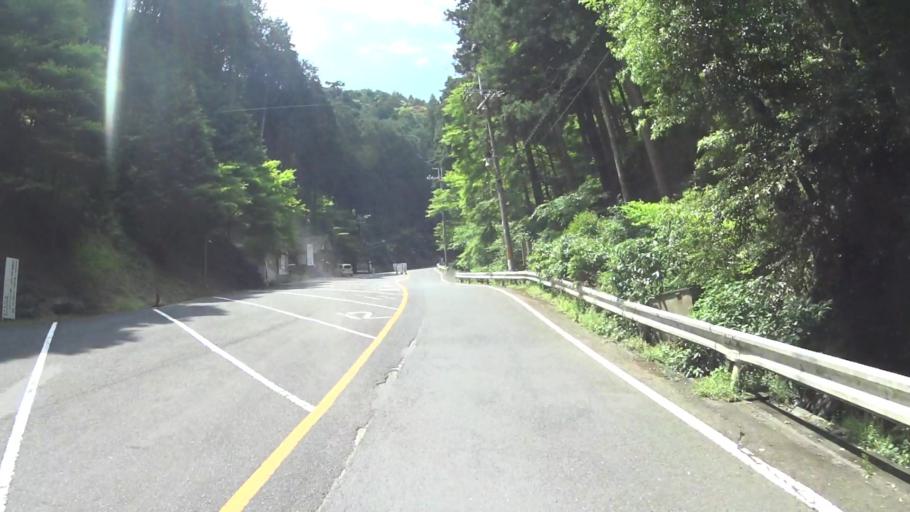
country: JP
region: Kyoto
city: Muko
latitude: 34.9385
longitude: 135.6467
